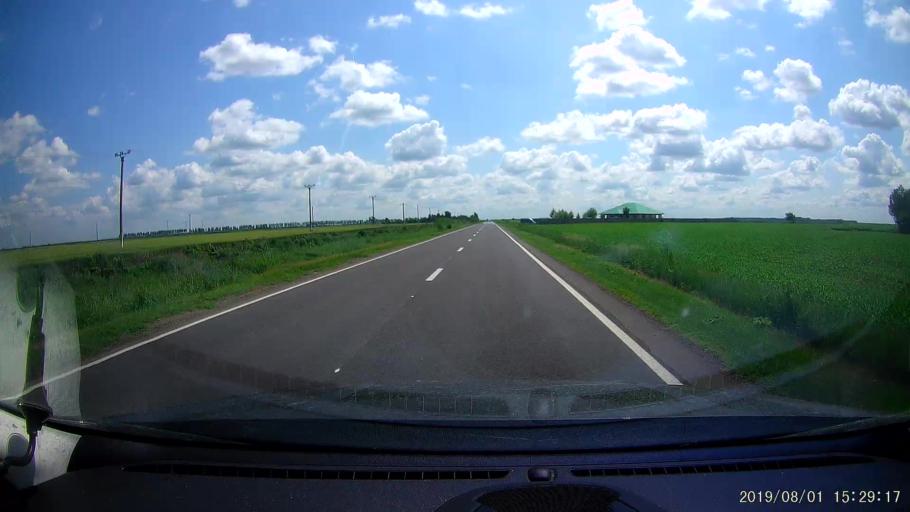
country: RO
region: Braila
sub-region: Comuna Viziru
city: Viziru
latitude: 44.9848
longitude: 27.6998
